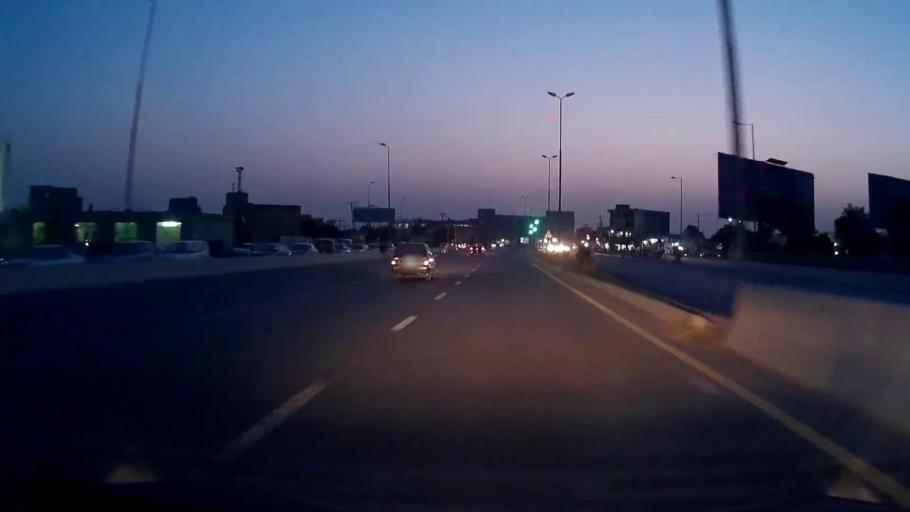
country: PK
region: Punjab
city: Lahore
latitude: 31.4976
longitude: 74.4227
